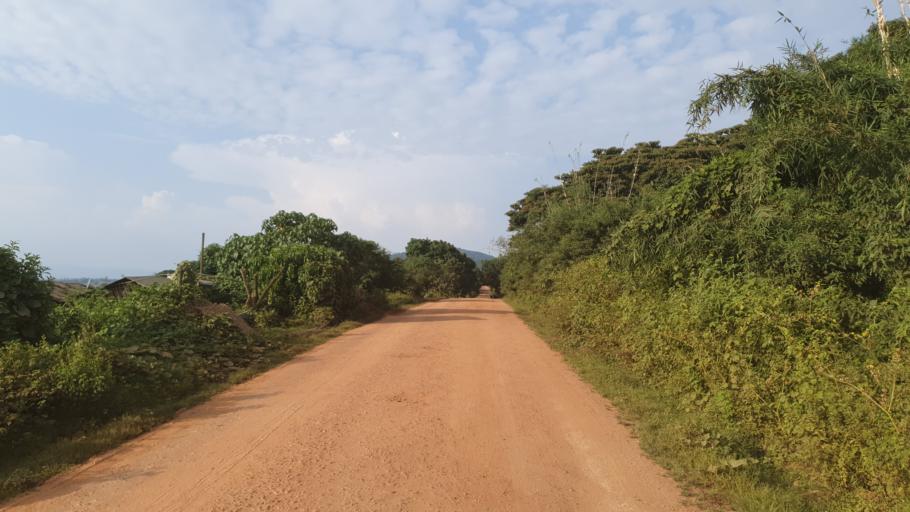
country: ET
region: Oromiya
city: Shambu
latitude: 9.4850
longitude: 36.5484
